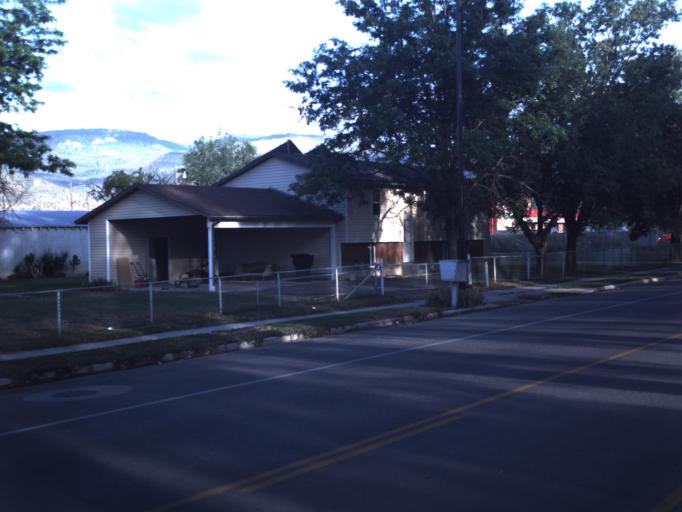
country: US
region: Utah
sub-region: Sanpete County
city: Ephraim
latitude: 39.3698
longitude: -111.5871
